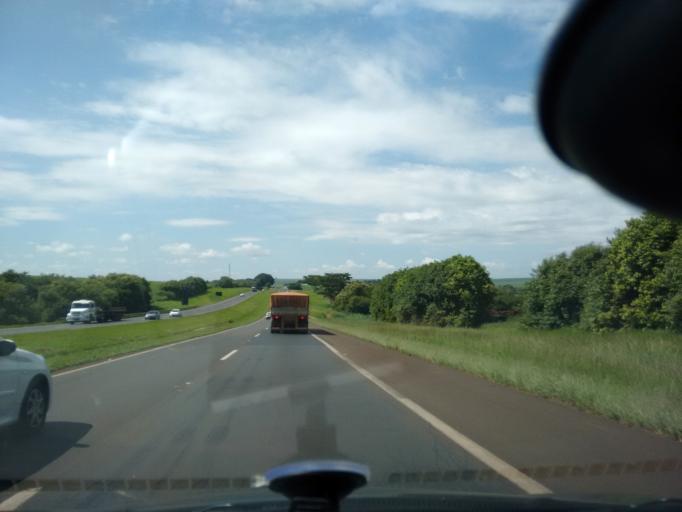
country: BR
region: Sao Paulo
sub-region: Araraquara
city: Araraquara
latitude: -21.8665
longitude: -48.1117
